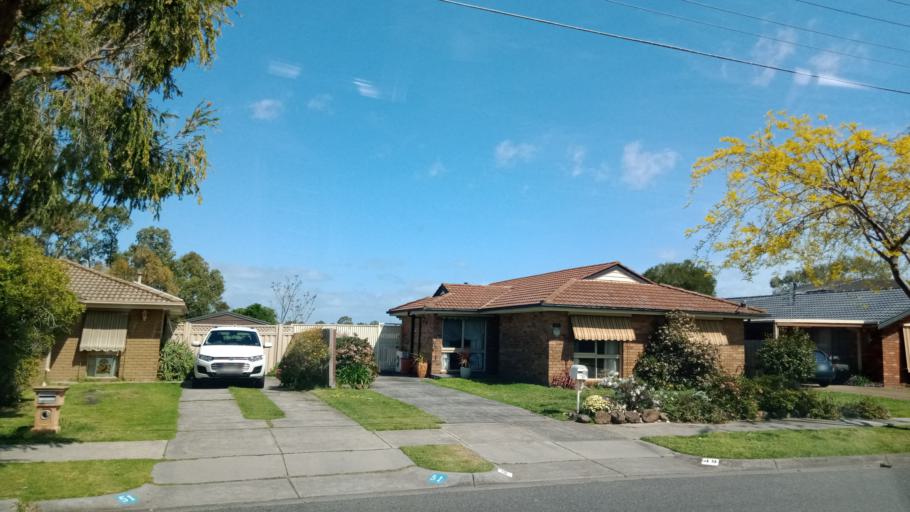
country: AU
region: Victoria
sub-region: Kingston
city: Chelsea Heights
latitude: -38.0364
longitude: 145.1308
